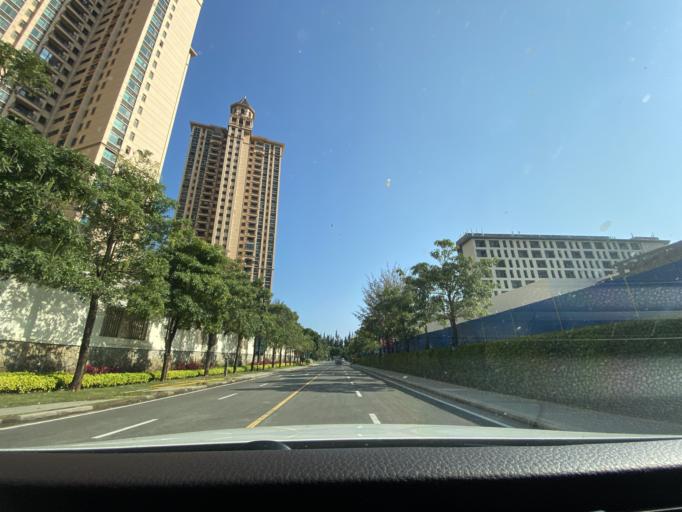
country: CN
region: Hainan
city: Yingzhou
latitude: 18.4117
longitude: 109.8862
